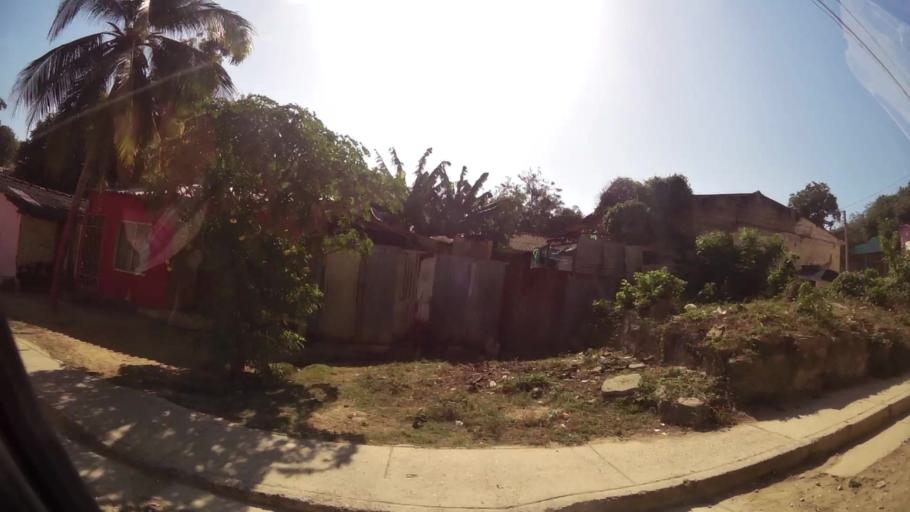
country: CO
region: Bolivar
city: Cartagena
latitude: 10.4268
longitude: -75.5328
